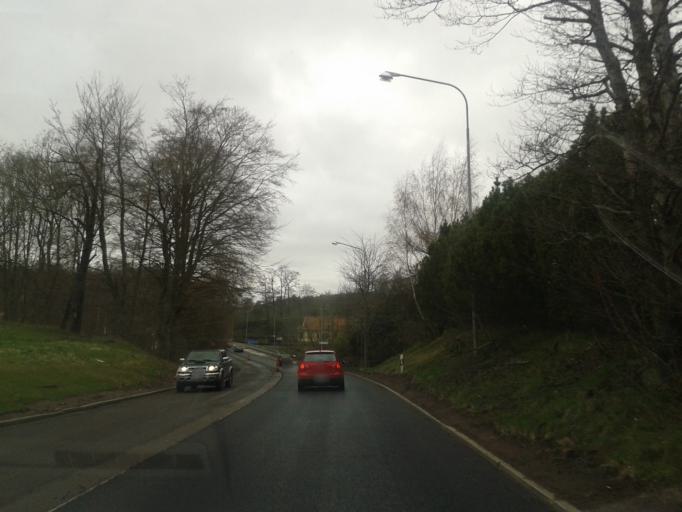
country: SE
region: Skane
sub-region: Angelholms Kommun
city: AEngelholm
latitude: 56.2759
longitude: 12.8539
